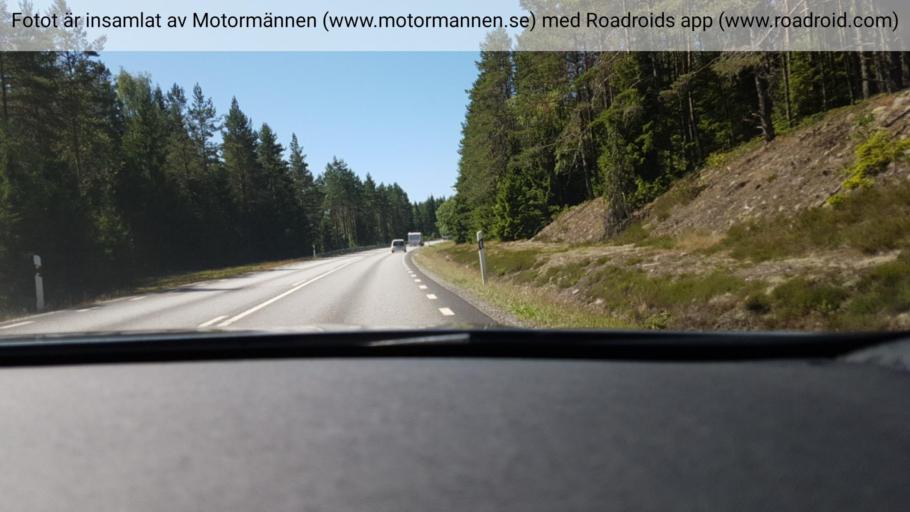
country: SE
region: Joenkoeping
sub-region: Gnosjo Kommun
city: Gnosjoe
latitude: 57.5721
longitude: 13.7121
